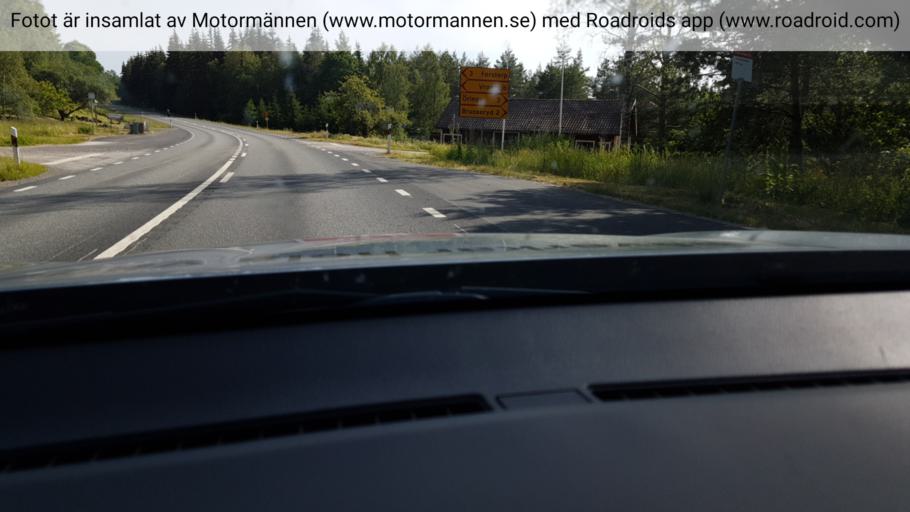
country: SE
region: Joenkoeping
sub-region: Aneby Kommun
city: Aneby
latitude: 57.8888
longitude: 14.8808
